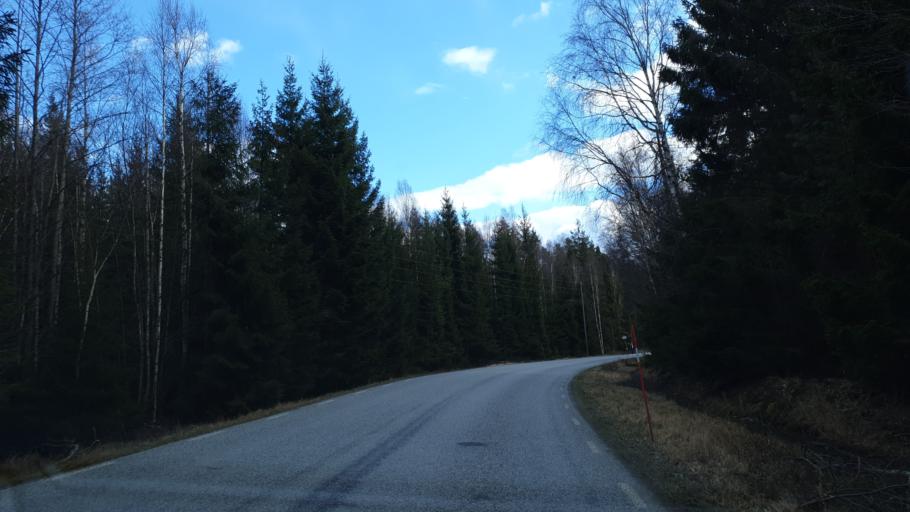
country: SE
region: Stockholm
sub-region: Varmdo Kommun
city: Hemmesta
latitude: 59.2374
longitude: 18.4789
